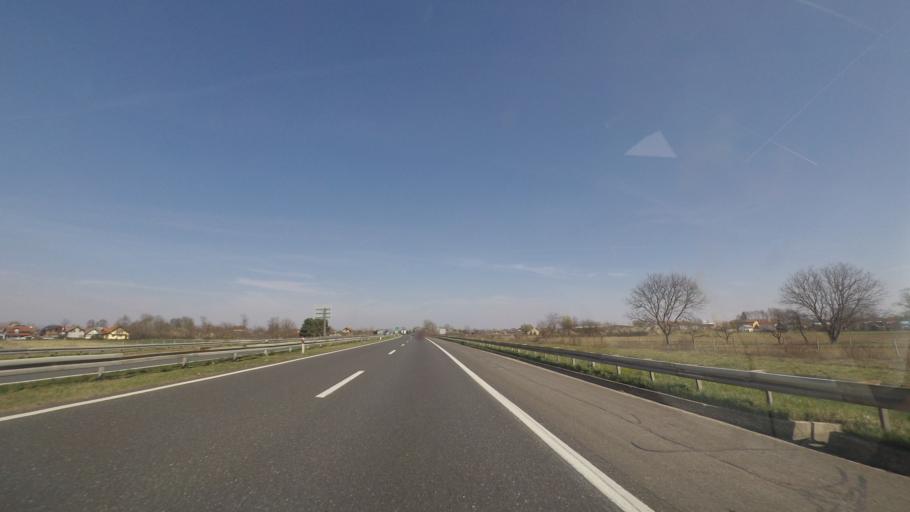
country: HR
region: Zagrebacka
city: Micevec
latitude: 45.7560
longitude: 16.0800
